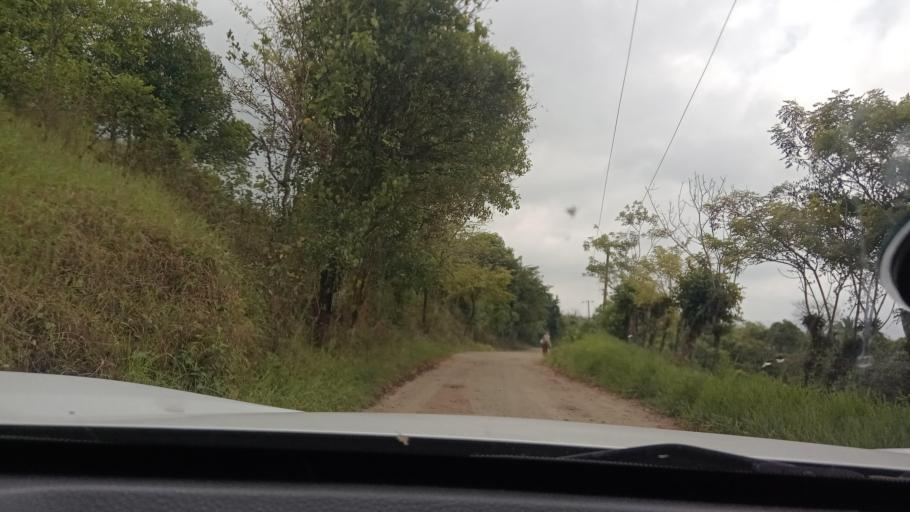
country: MX
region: Tabasco
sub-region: Huimanguillo
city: Francisco Rueda
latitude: 17.5641
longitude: -94.0227
